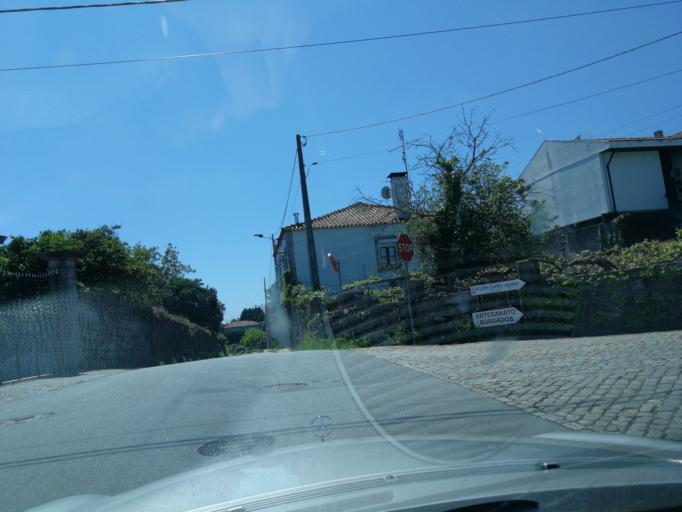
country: PT
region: Viana do Castelo
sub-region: Viana do Castelo
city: Meadela
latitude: 41.7280
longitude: -8.7885
